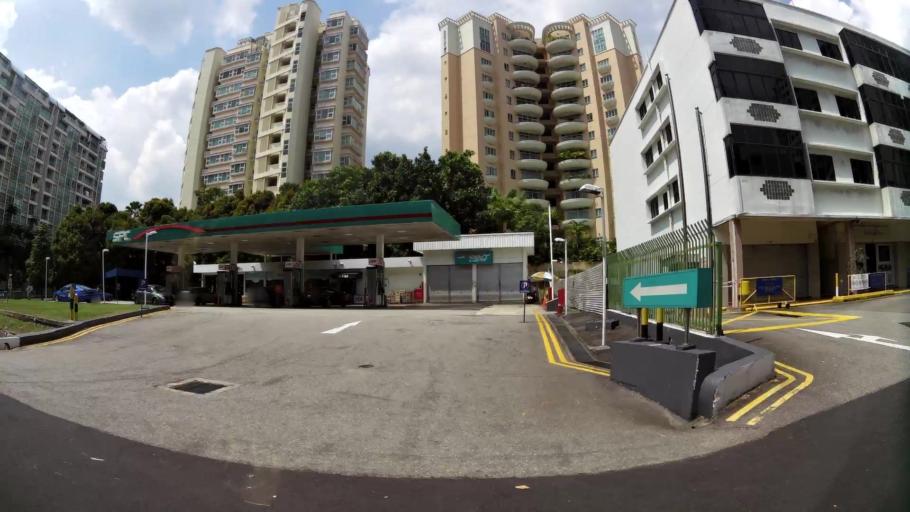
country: SG
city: Singapore
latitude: 1.2932
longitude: 103.8263
